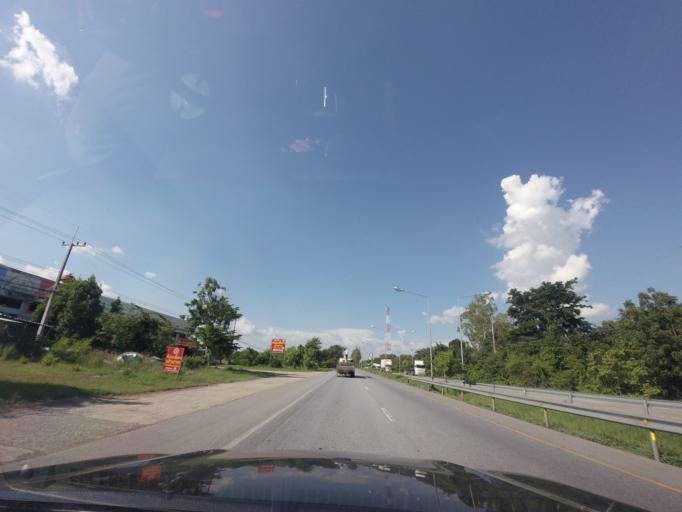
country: TH
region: Nakhon Ratchasima
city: Sida
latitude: 15.5344
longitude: 102.5445
